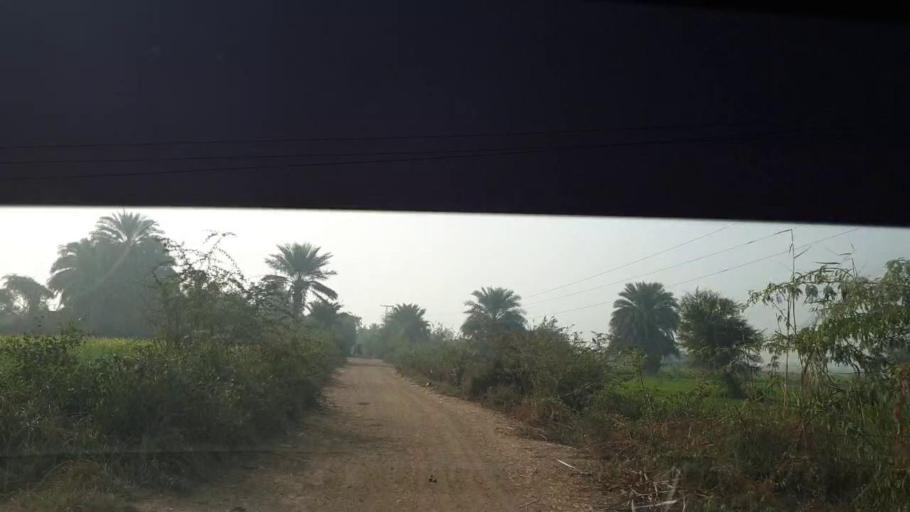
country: PK
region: Sindh
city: Berani
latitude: 25.7800
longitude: 68.7896
